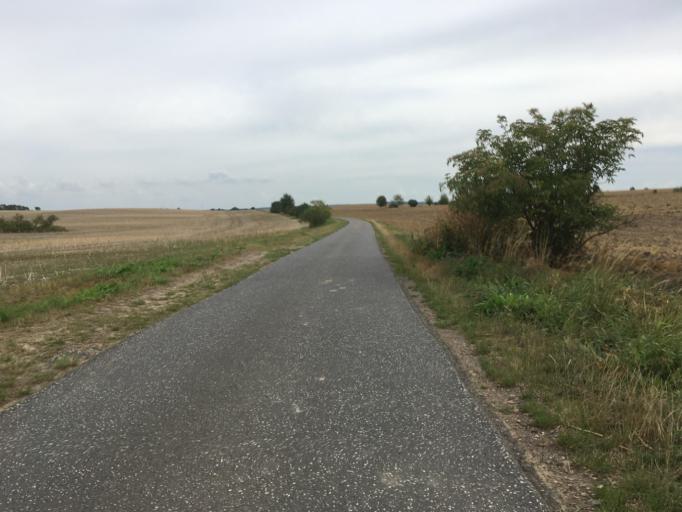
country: DE
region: Brandenburg
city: Gerswalde
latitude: 53.1554
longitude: 13.7922
